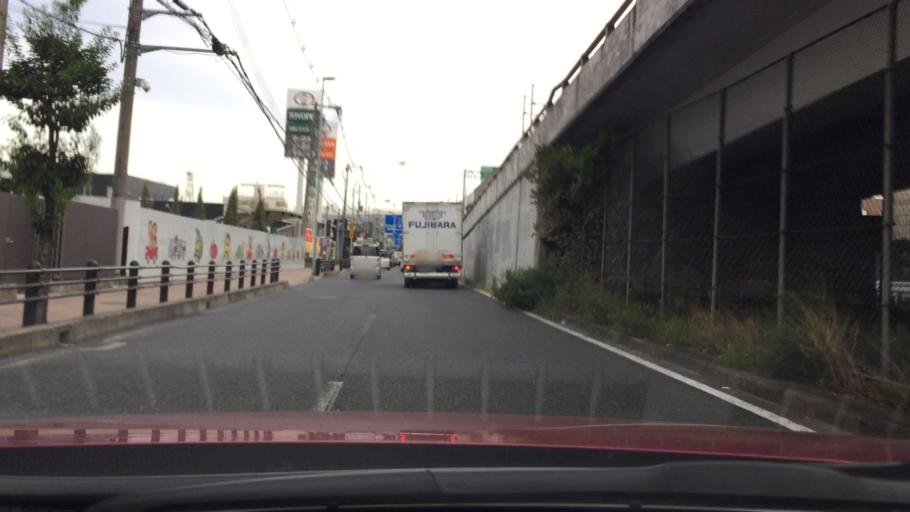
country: JP
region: Osaka
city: Kadoma
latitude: 34.7500
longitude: 135.5777
